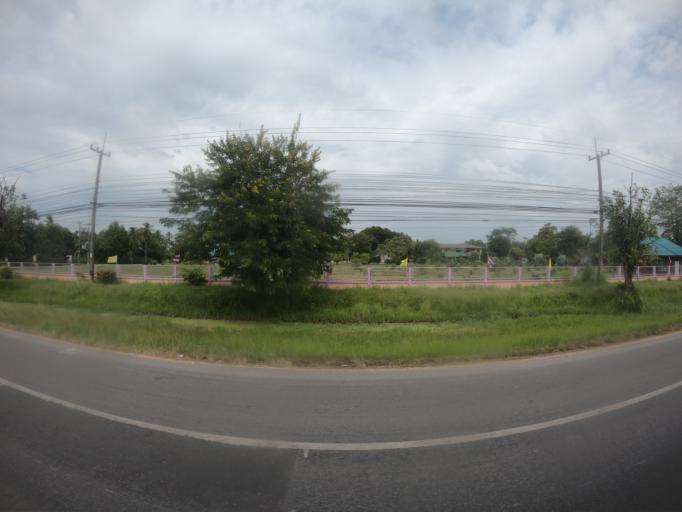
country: TH
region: Roi Et
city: Roi Et
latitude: 16.0705
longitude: 103.6020
